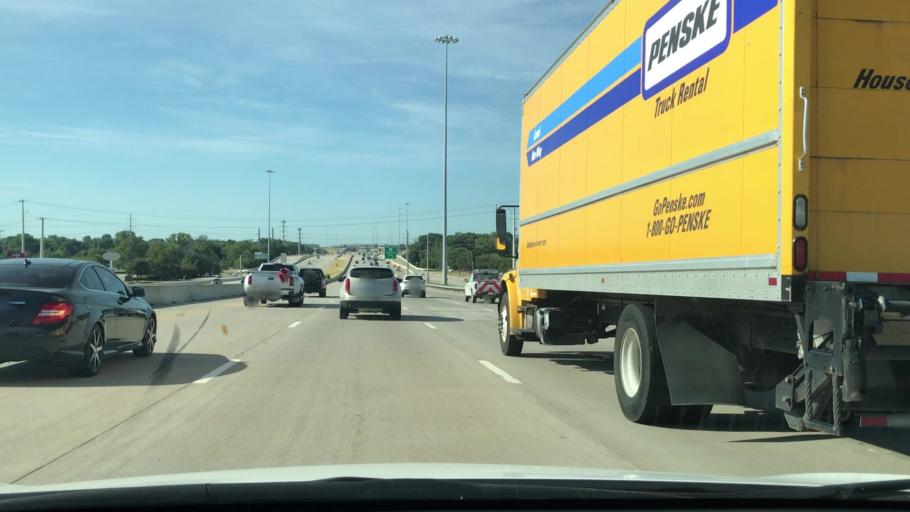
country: US
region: Texas
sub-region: Collin County
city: McKinney
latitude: 33.1913
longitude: -96.6374
